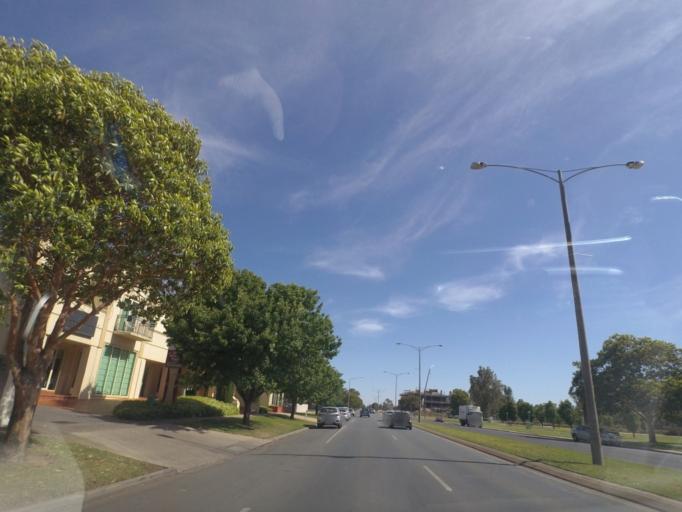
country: AU
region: Victoria
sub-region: Greater Shepparton
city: Shepparton
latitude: -36.3883
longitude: 145.3979
